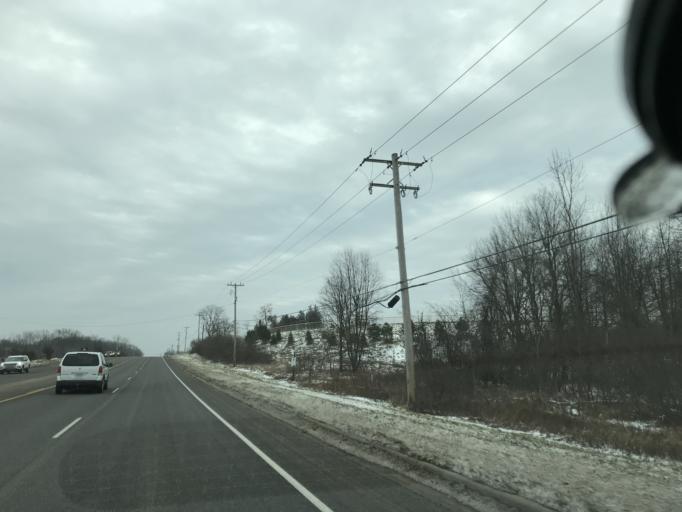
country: US
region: Michigan
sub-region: Kent County
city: Rockford
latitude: 43.1170
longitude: -85.5931
